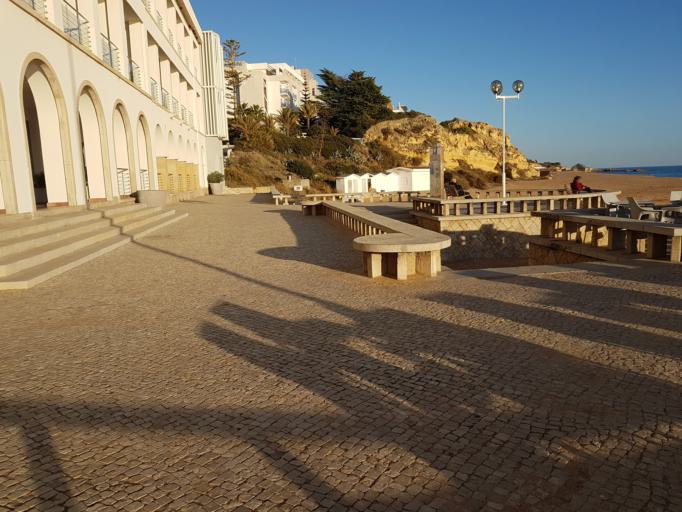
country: PT
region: Faro
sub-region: Albufeira
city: Albufeira
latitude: 37.0859
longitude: -8.2437
